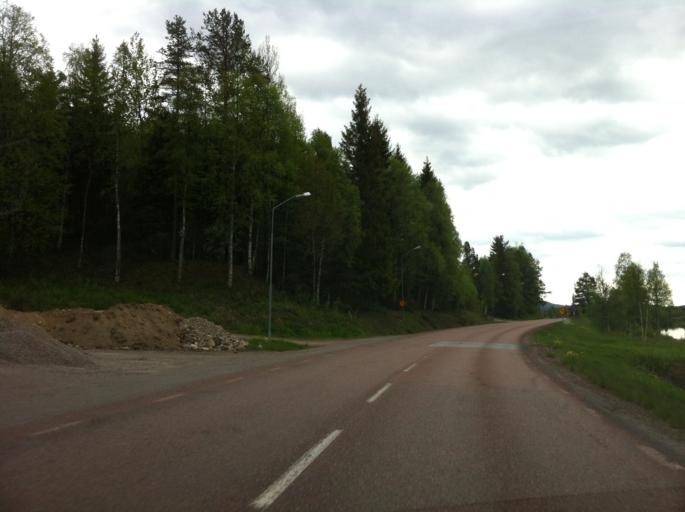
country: SE
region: Dalarna
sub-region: Malung-Saelens kommun
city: Malung
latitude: 61.0910
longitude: 13.3195
